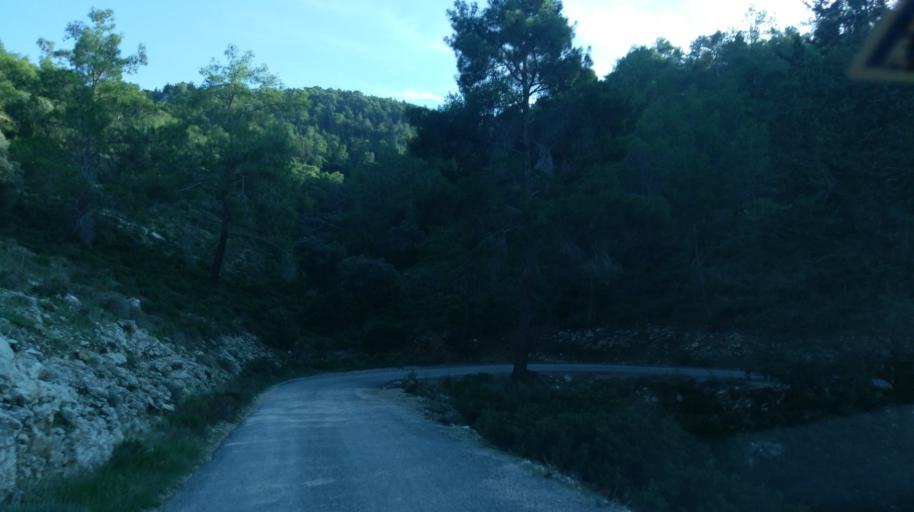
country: CY
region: Ammochostos
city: Lefkonoiko
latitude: 35.3259
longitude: 33.6080
